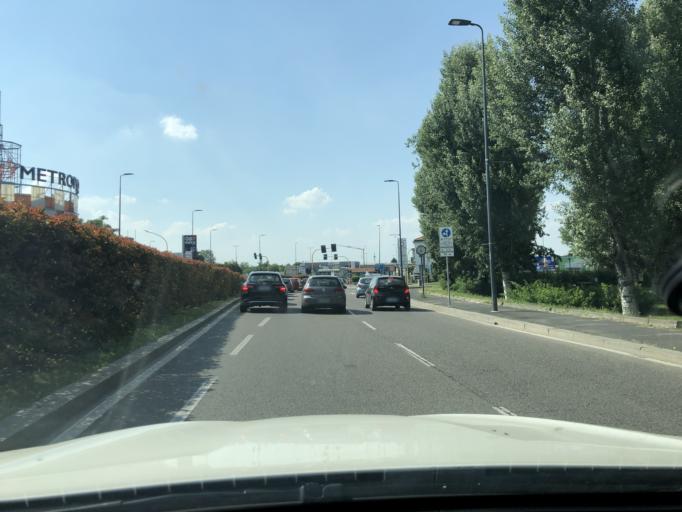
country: IT
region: Lombardy
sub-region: Citta metropolitana di Milano
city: Novate Milanese
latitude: 45.5203
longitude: 9.1518
